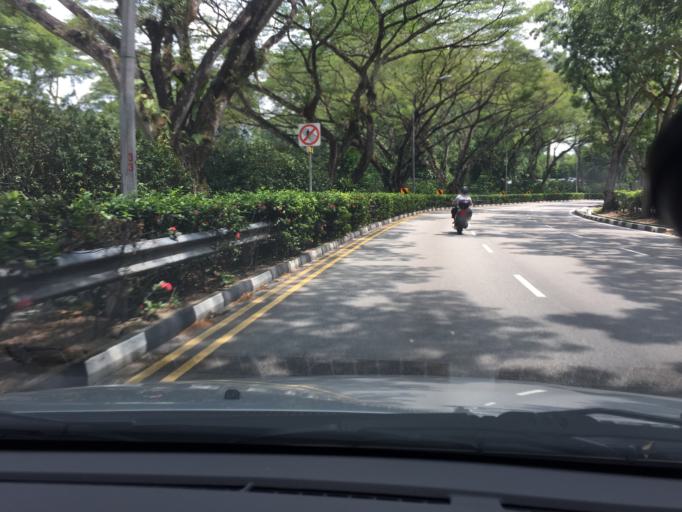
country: SG
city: Singapore
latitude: 1.3064
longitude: 103.8138
